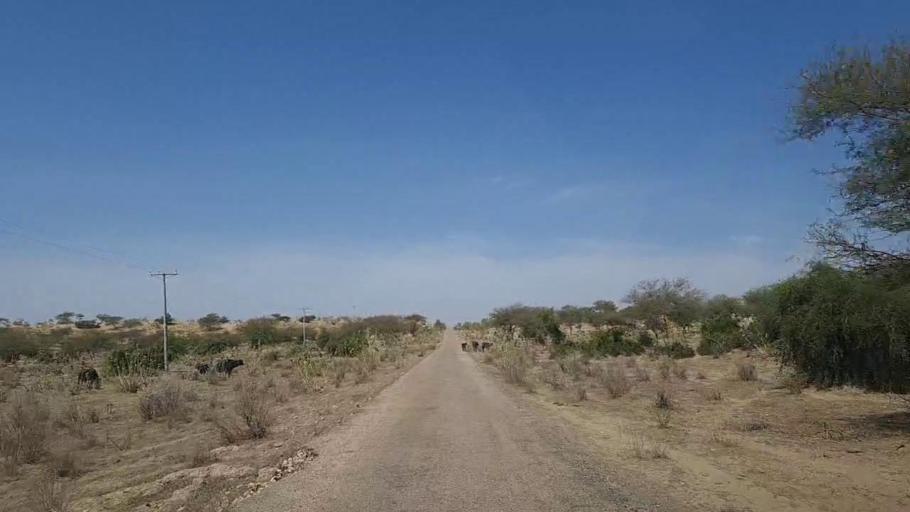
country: PK
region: Sindh
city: Mithi
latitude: 24.8559
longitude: 69.6700
